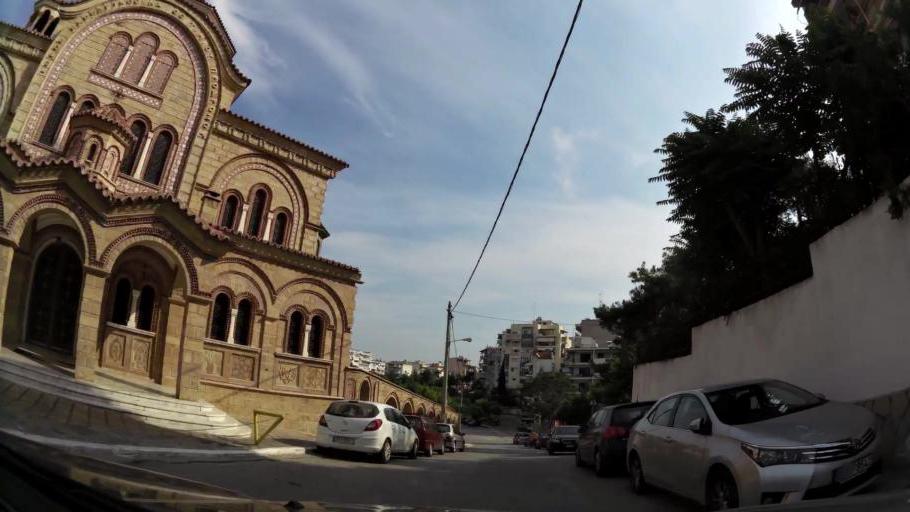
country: GR
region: Central Macedonia
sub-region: Nomos Thessalonikis
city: Sykies
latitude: 40.6549
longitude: 22.9488
